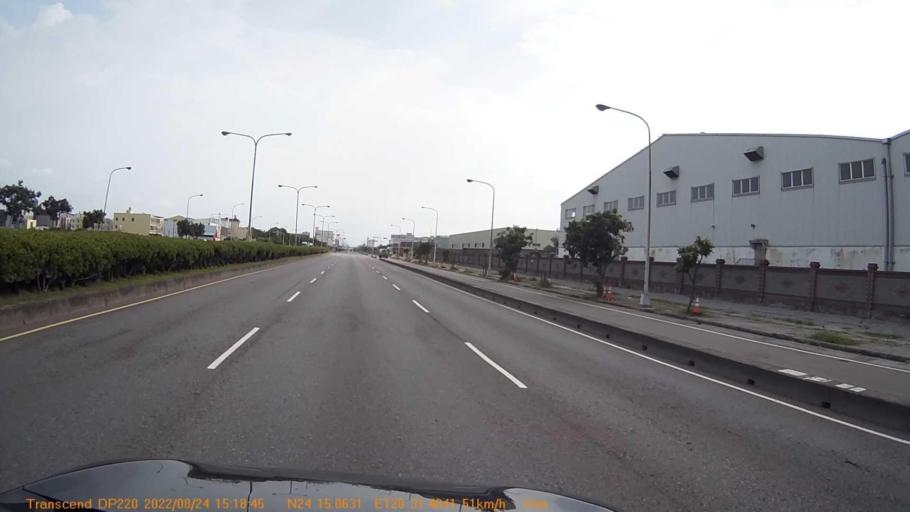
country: TW
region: Taiwan
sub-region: Changhua
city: Chang-hua
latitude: 24.2507
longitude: 120.5232
